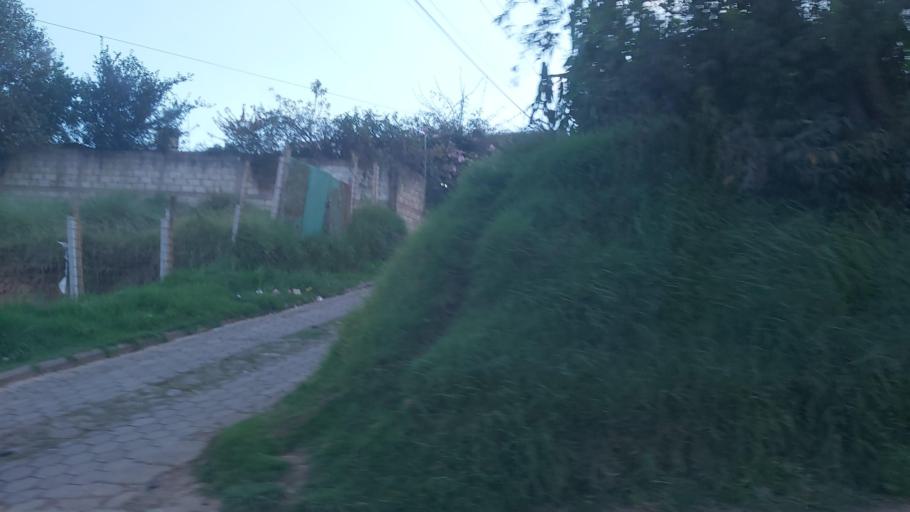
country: GT
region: Quetzaltenango
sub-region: Municipio de La Esperanza
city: La Esperanza
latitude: 14.8471
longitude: -91.5506
